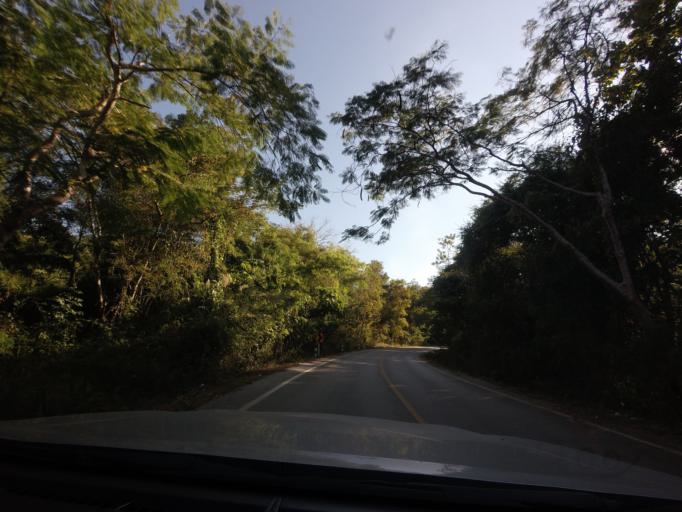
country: TH
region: Lampang
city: Chae Hom
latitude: 18.5928
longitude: 99.6289
